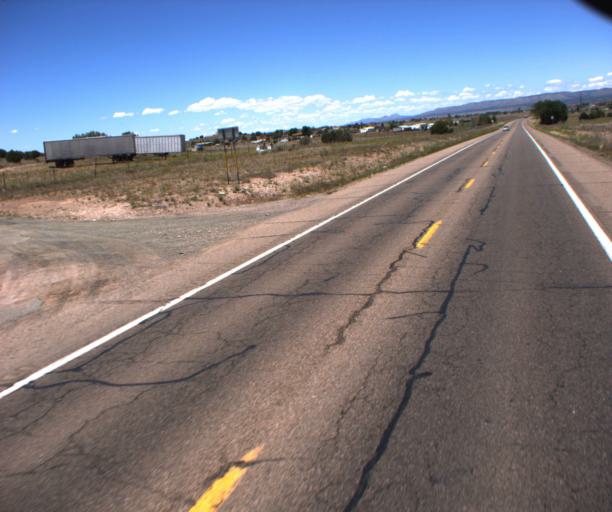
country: US
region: Arizona
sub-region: Yavapai County
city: Paulden
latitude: 34.8379
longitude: -112.4626
